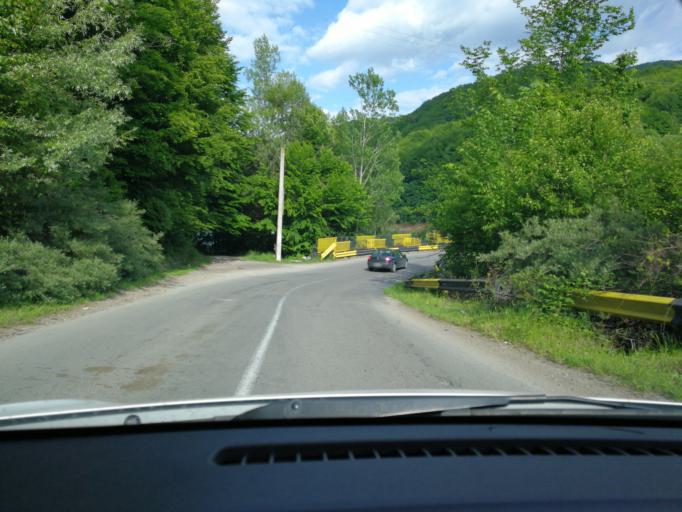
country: RO
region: Prahova
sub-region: Comuna Sotrile
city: Sotrile
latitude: 45.2550
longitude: 25.7407
